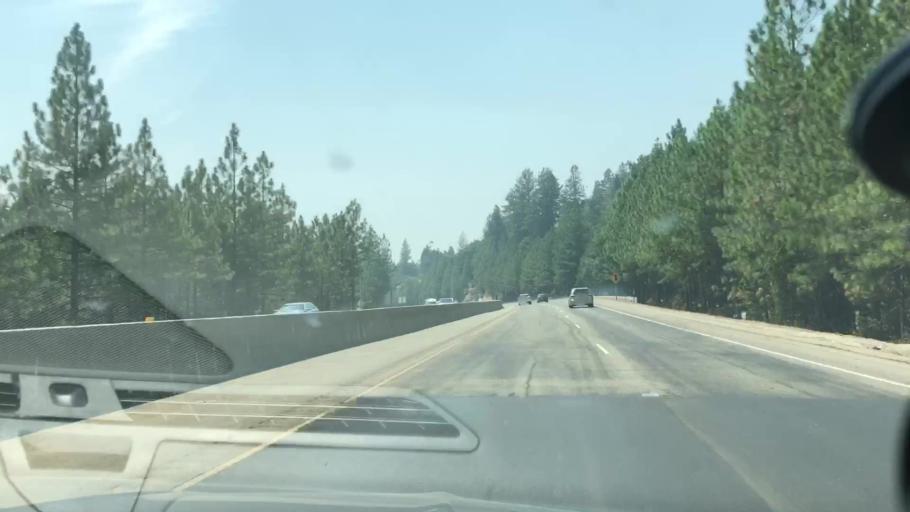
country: US
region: California
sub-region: El Dorado County
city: Pollock Pines
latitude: 38.7485
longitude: -120.6180
